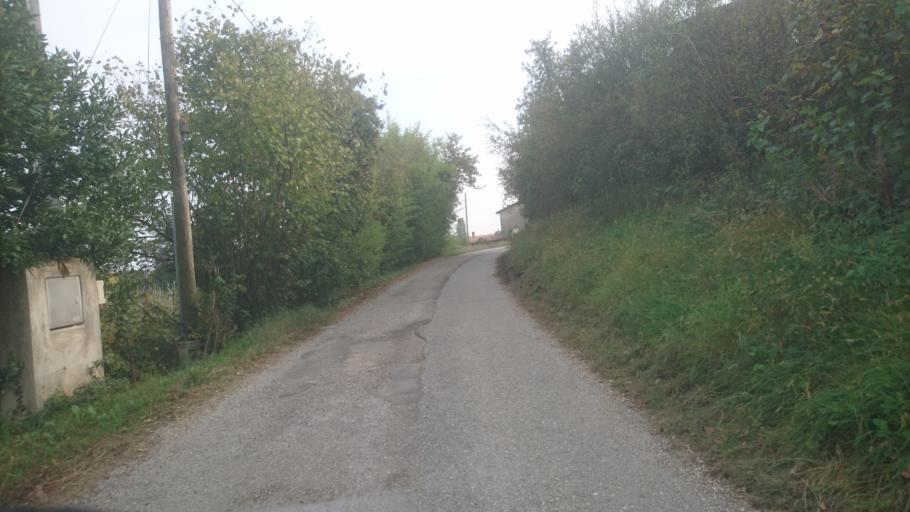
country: IT
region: Veneto
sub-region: Provincia di Vicenza
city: Montegalda
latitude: 45.4639
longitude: 11.6677
